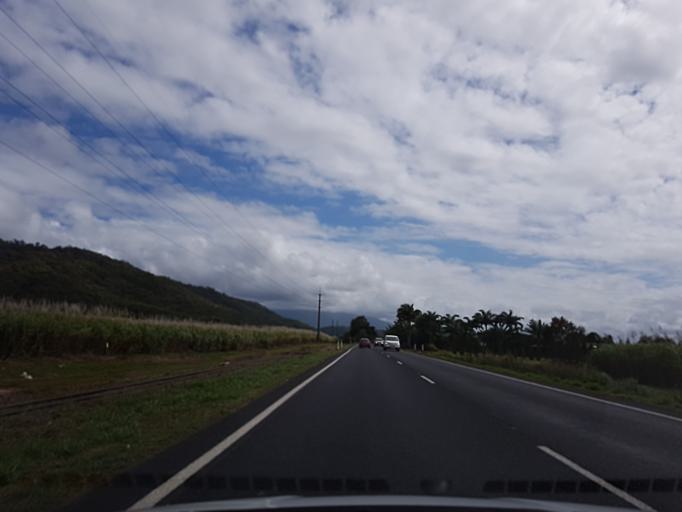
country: AU
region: Queensland
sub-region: Cairns
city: Port Douglas
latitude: -16.4950
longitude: 145.4251
